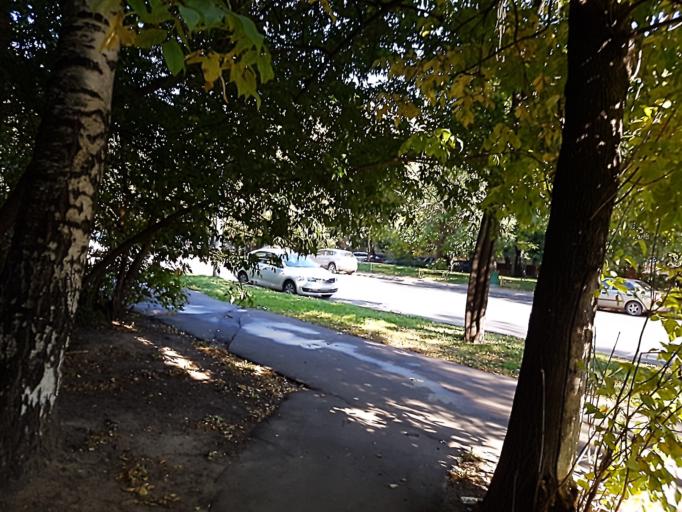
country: RU
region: Moskovskaya
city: Novogireyevo
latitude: 55.7522
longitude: 37.8022
